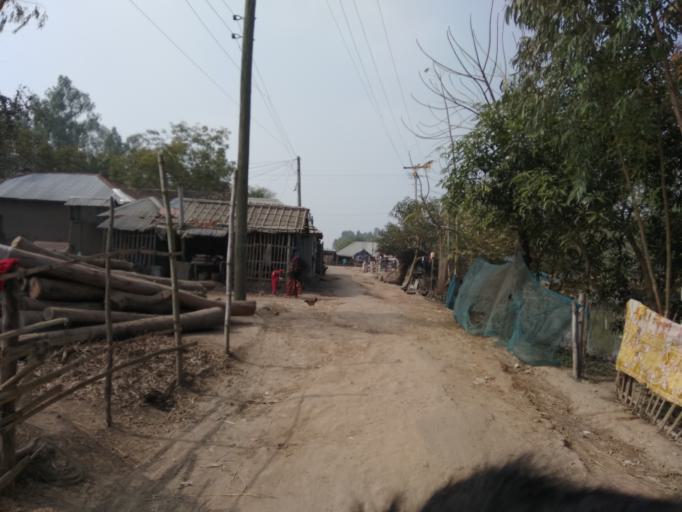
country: BD
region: Rajshahi
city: Bogra
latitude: 24.4802
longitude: 89.2682
